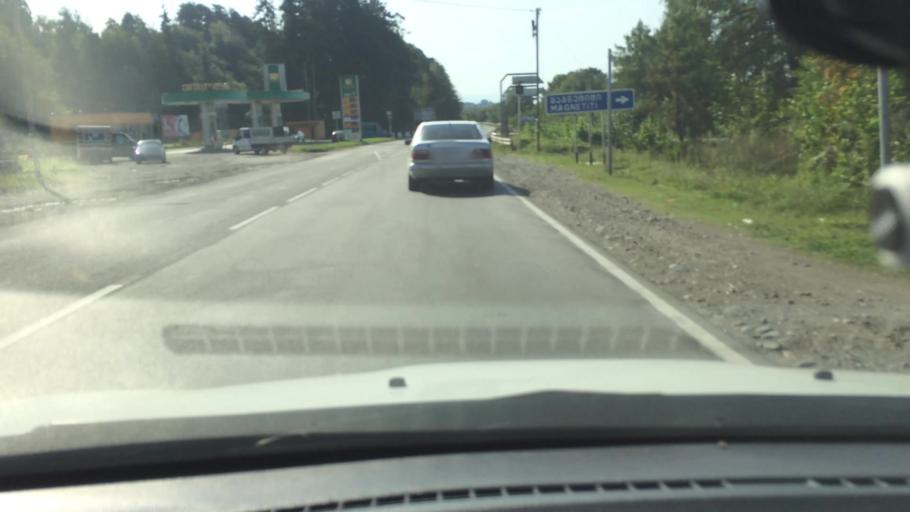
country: GE
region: Guria
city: Urek'i
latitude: 41.9932
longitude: 41.7812
